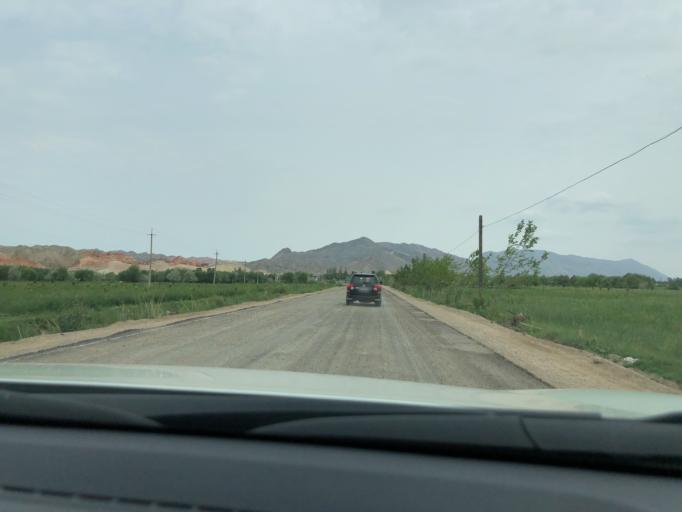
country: TJ
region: Viloyati Sughd
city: Isfara
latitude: 40.1526
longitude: 70.6248
